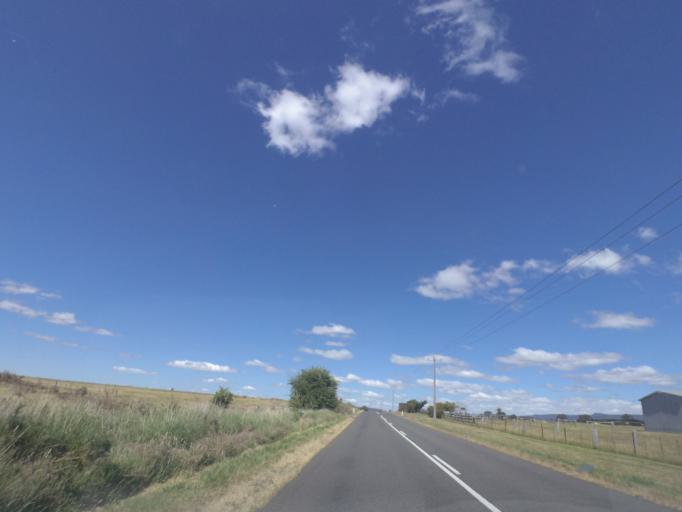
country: AU
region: Victoria
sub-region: Mount Alexander
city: Castlemaine
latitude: -37.2897
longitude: 144.4754
